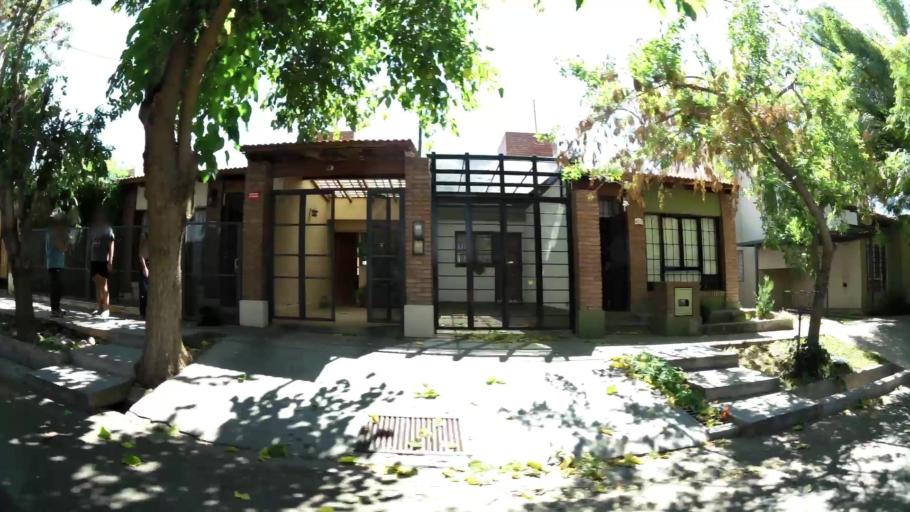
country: AR
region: Mendoza
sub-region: Departamento de Godoy Cruz
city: Godoy Cruz
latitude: -32.9780
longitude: -68.8558
